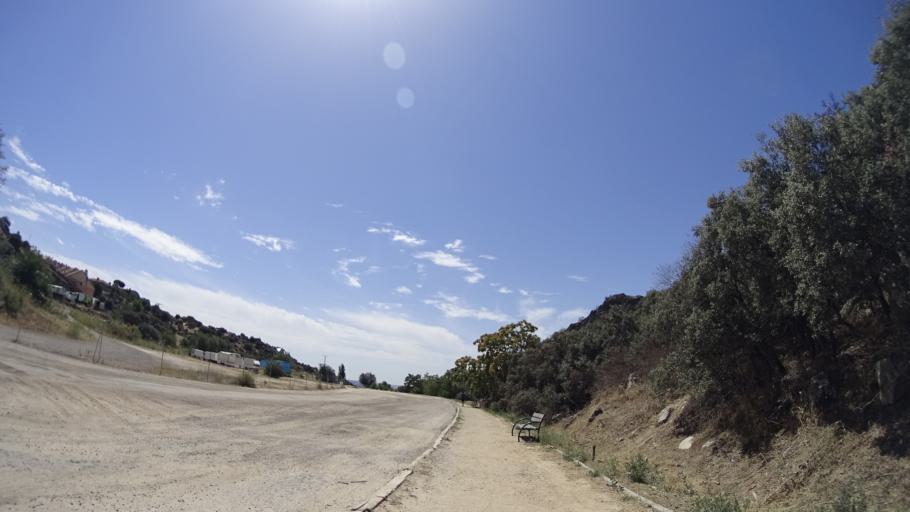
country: ES
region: Madrid
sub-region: Provincia de Madrid
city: Torrelodones
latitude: 40.5732
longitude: -3.9311
